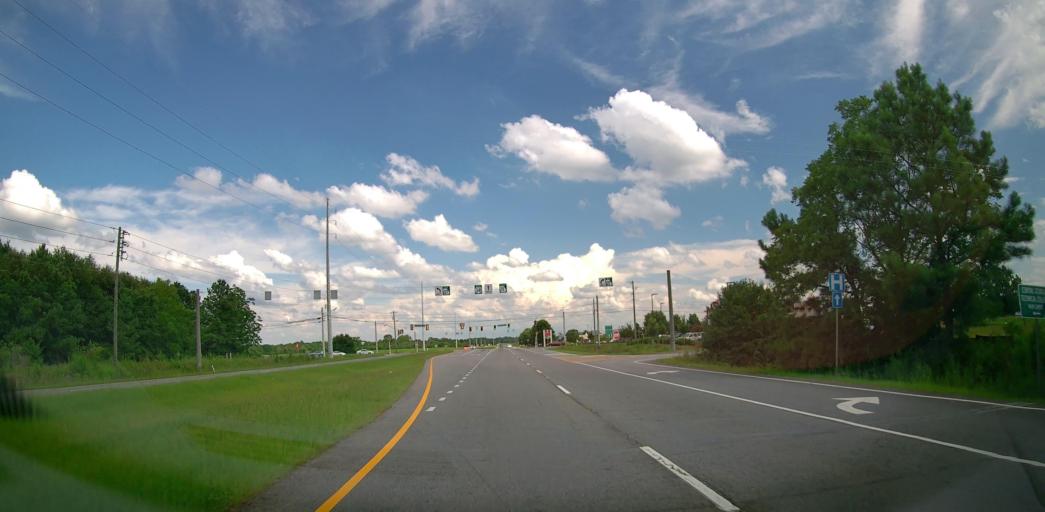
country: US
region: Georgia
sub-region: Houston County
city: Perry
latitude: 32.4762
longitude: -83.7066
